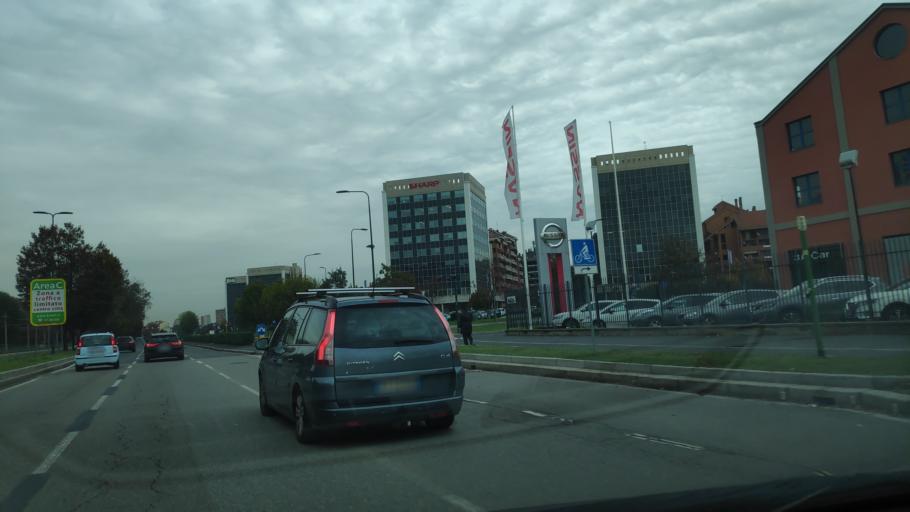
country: IT
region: Lombardy
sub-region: Citta metropolitana di Milano
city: Rozzano
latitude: 45.4148
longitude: 9.1753
